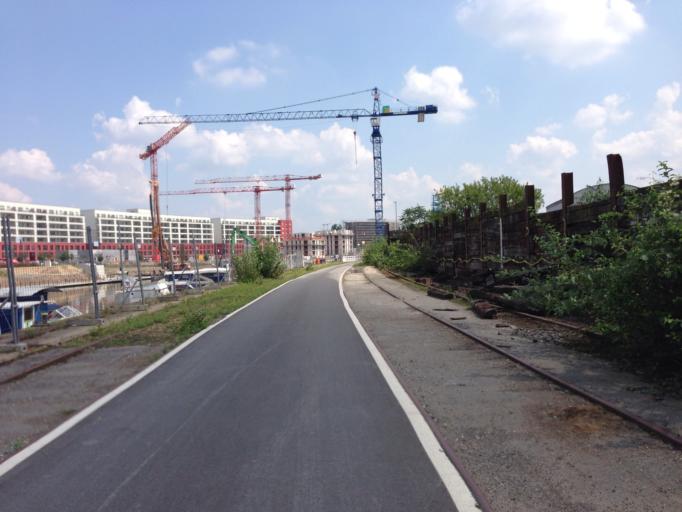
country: DE
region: Hesse
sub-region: Regierungsbezirk Darmstadt
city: Offenbach
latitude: 50.1134
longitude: 8.7482
